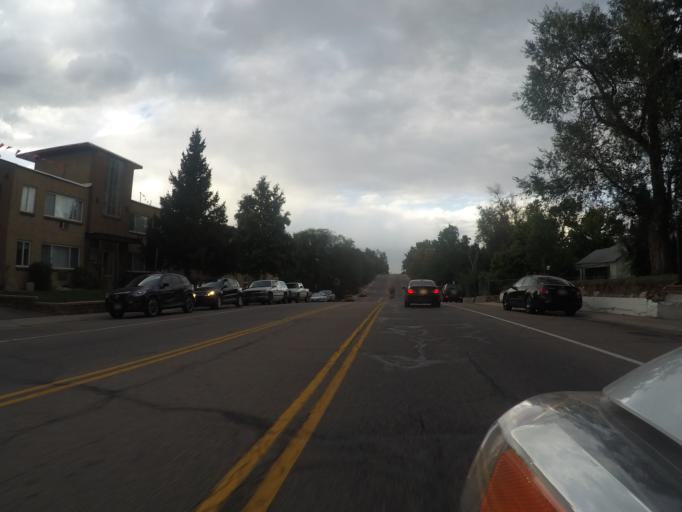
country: US
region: Colorado
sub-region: Arapahoe County
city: Littleton
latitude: 39.6163
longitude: -105.0068
